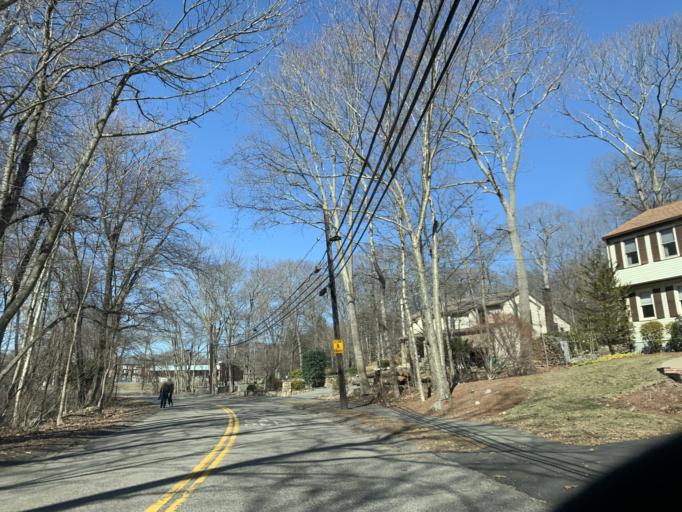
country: US
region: Massachusetts
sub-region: Norfolk County
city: Westwood
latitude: 42.1918
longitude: -71.2223
